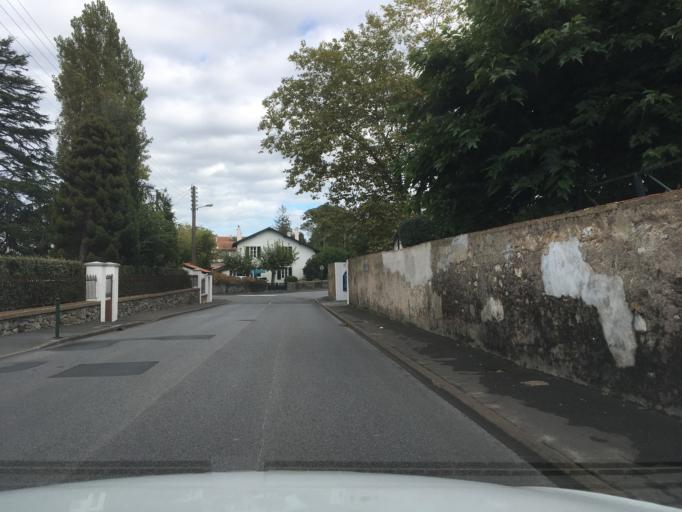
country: FR
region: Aquitaine
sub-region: Departement des Pyrenees-Atlantiques
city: Biarritz
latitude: 43.4629
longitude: -1.5600
